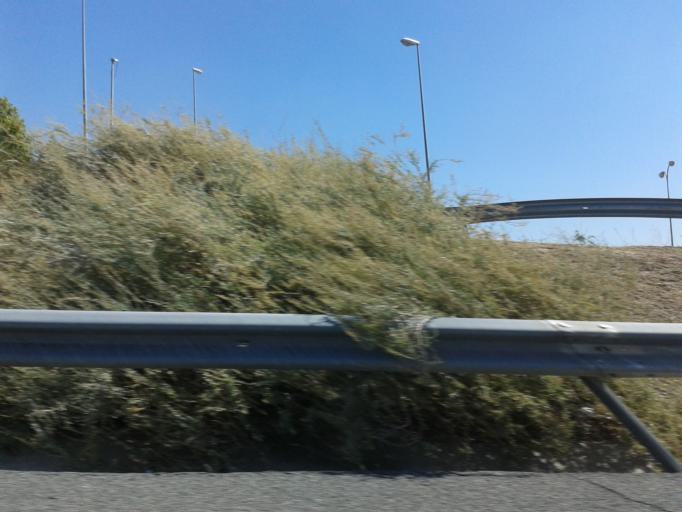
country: ES
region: Madrid
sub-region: Provincia de Madrid
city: Barajas de Madrid
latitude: 40.4742
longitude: -3.5741
